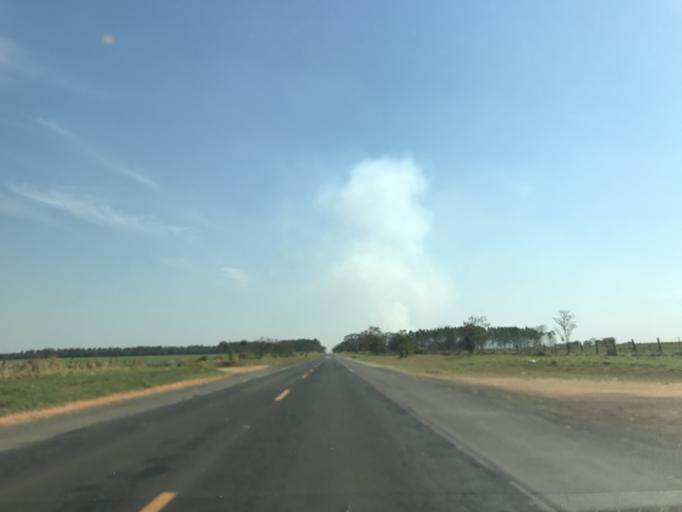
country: BR
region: Sao Paulo
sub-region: Penapolis
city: Penapolis
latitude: -21.3692
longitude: -50.0773
